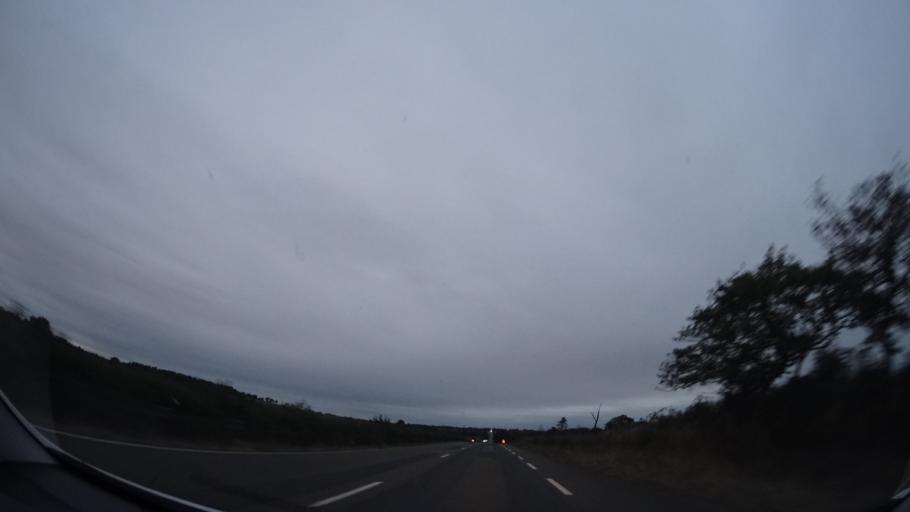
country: FR
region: Pays de la Loire
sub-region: Departement de la Mayenne
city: Argentre
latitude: 48.0658
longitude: -0.6417
